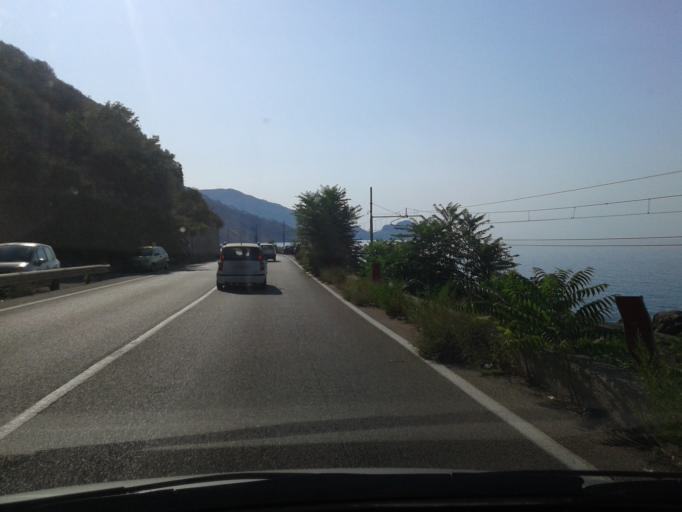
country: IT
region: Sicily
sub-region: Palermo
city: Pollina
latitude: 38.0166
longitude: 14.1245
